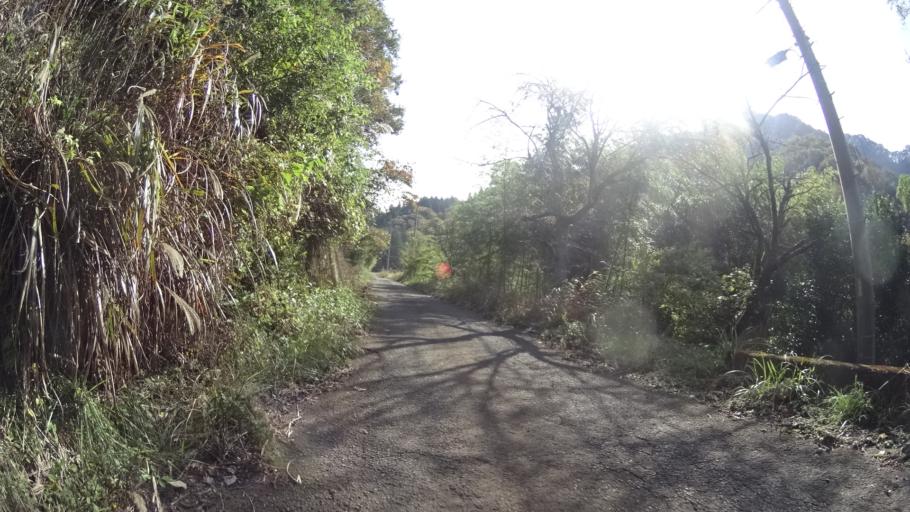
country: JP
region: Yamanashi
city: Otsuki
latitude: 35.5823
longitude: 138.9730
